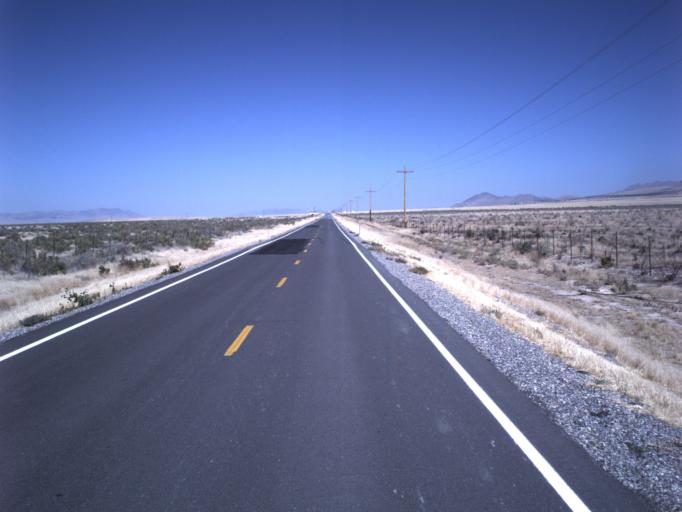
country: US
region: Utah
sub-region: Tooele County
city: Grantsville
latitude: 40.3597
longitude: -112.7458
